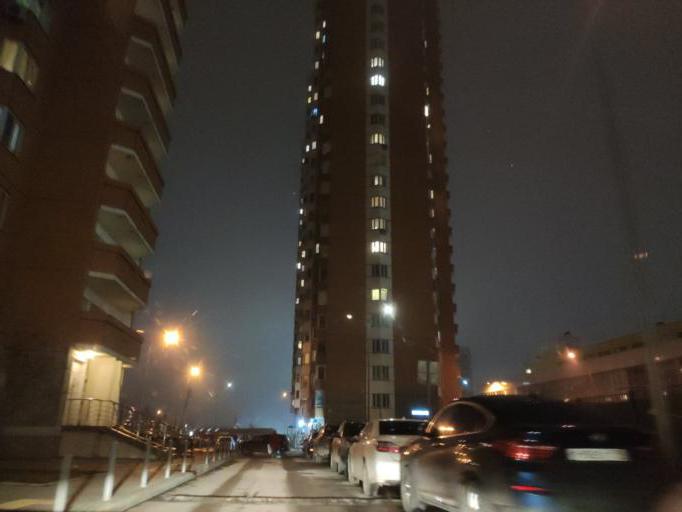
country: RU
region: Moscow
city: Kotlovka
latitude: 55.6713
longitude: 37.6112
